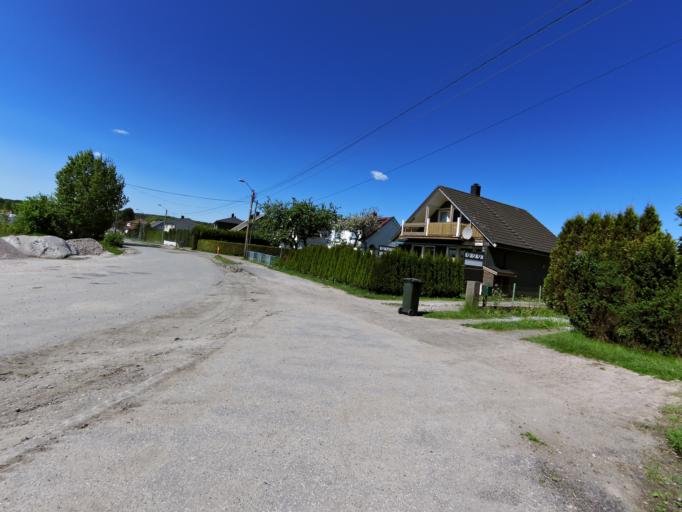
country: NO
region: Ostfold
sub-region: Fredrikstad
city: Fredrikstad
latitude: 59.2326
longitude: 10.9837
